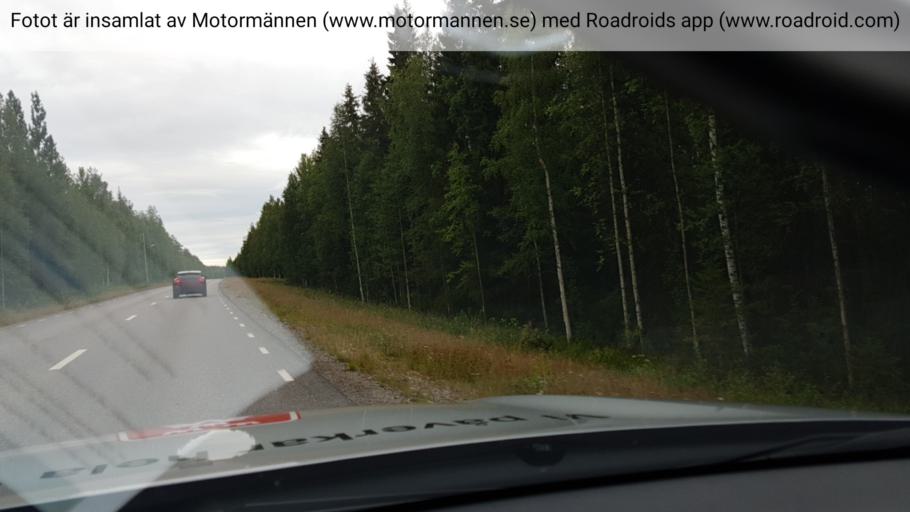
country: SE
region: Norrbotten
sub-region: Overkalix Kommun
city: OEverkalix
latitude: 66.5651
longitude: 22.7615
